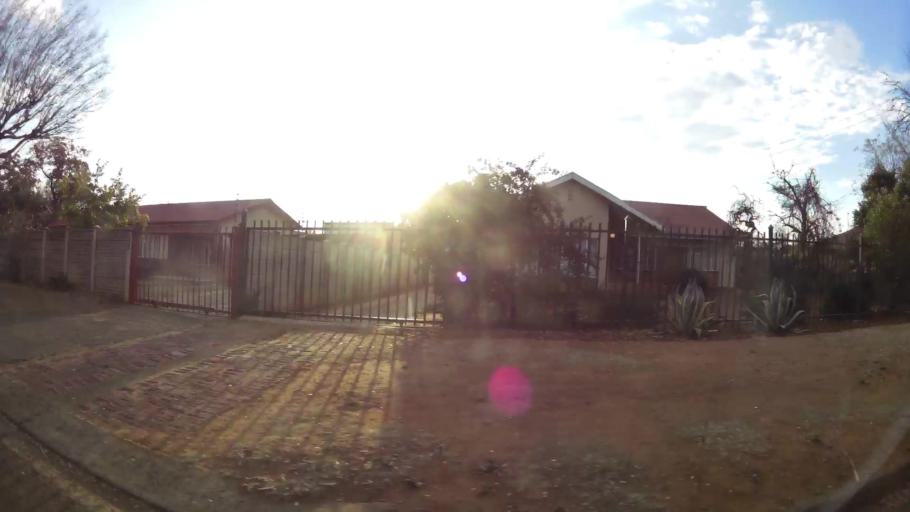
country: ZA
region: Orange Free State
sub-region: Mangaung Metropolitan Municipality
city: Bloemfontein
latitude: -29.1391
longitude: 26.1950
